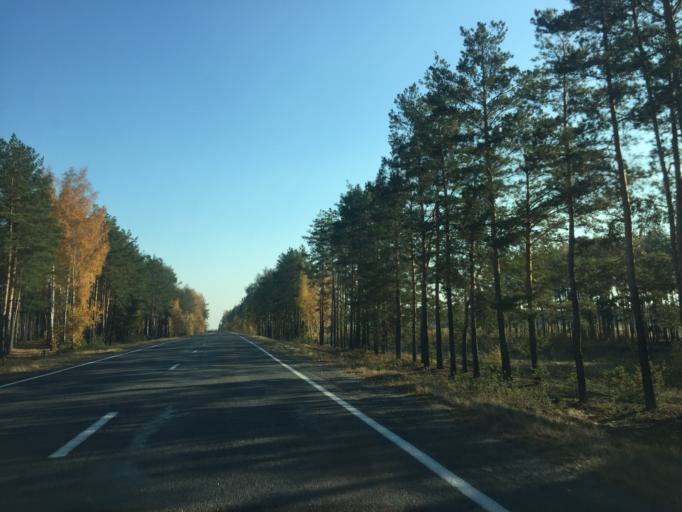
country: BY
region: Gomel
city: Dobrush
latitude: 52.3344
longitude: 31.2367
